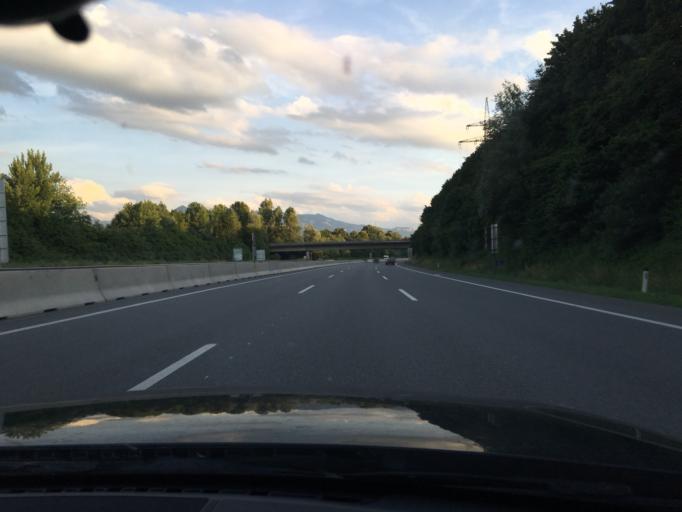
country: AT
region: Vorarlberg
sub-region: Politischer Bezirk Bregenz
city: Lauterach
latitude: 47.4724
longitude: 9.7389
